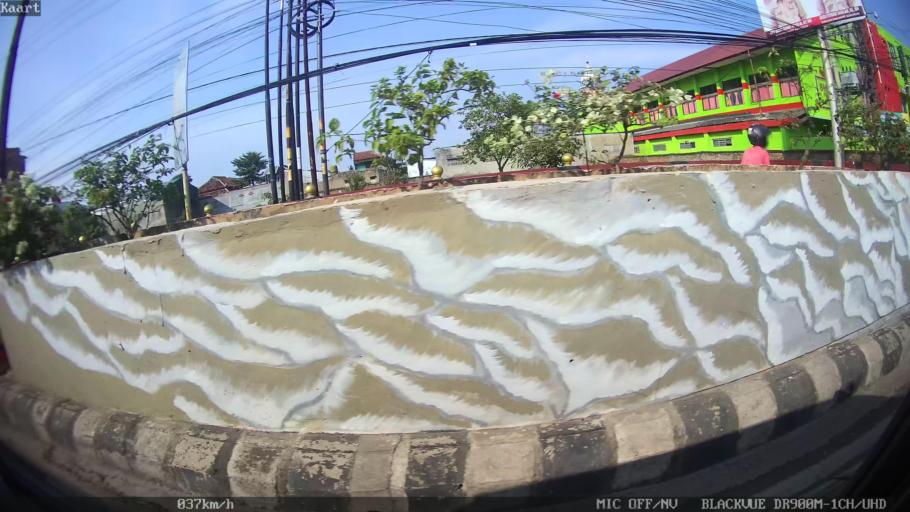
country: ID
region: Lampung
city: Kedaton
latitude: -5.3733
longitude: 105.2400
